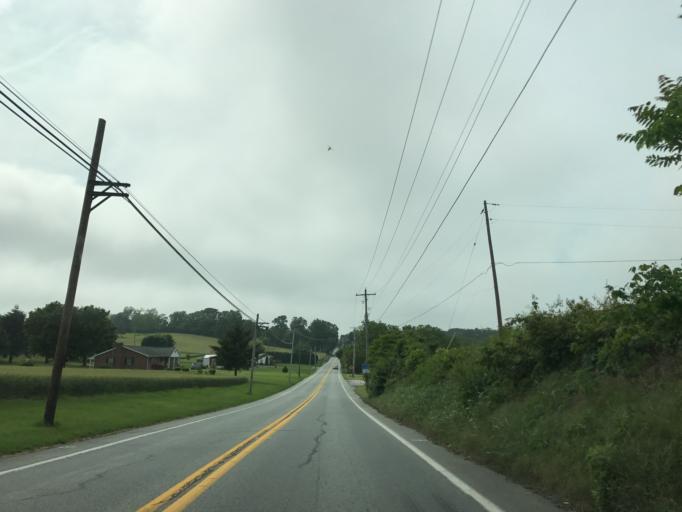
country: US
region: Pennsylvania
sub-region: York County
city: Windsor
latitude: 39.8846
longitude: -76.5435
